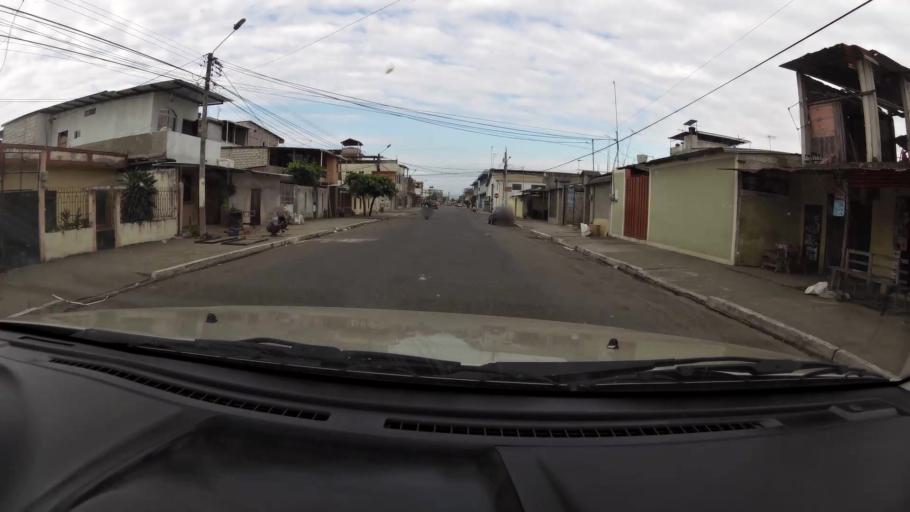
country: EC
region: El Oro
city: Machala
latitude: -3.2510
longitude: -79.9515
